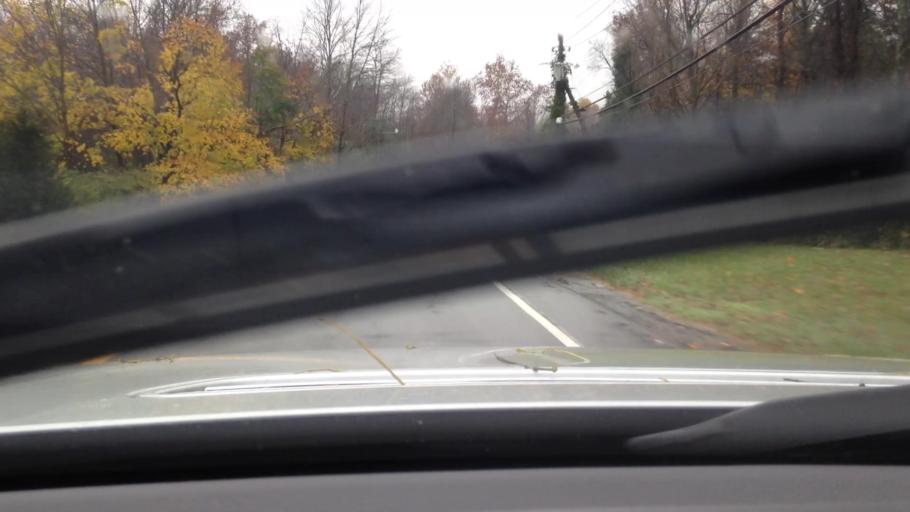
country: US
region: New York
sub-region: Orange County
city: West Point
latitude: 41.3874
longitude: -73.9345
